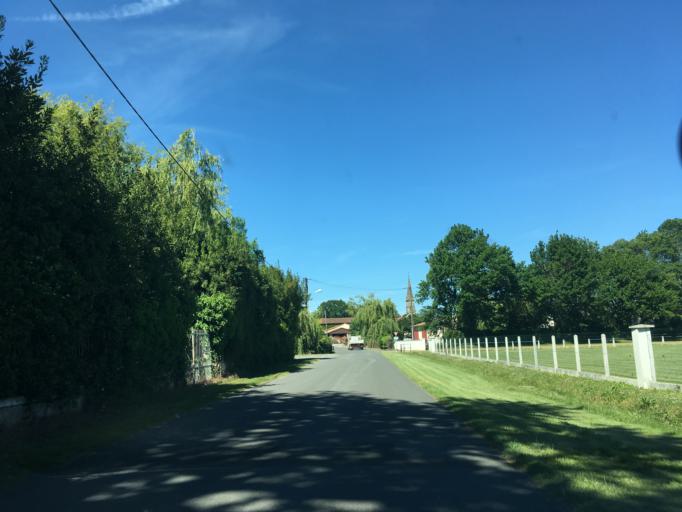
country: FR
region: Aquitaine
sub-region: Departement de la Gironde
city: Lesparre-Medoc
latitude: 45.3206
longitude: -0.8811
